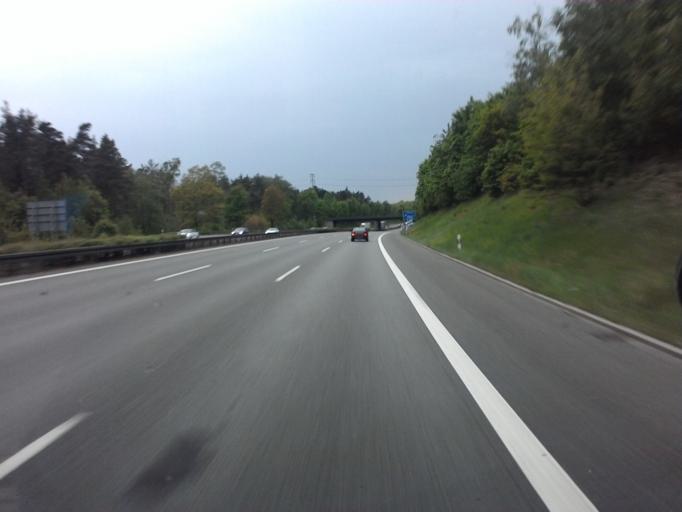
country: DE
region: Bavaria
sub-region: Regierungsbezirk Mittelfranken
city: Schwaig
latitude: 49.4667
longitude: 11.1914
